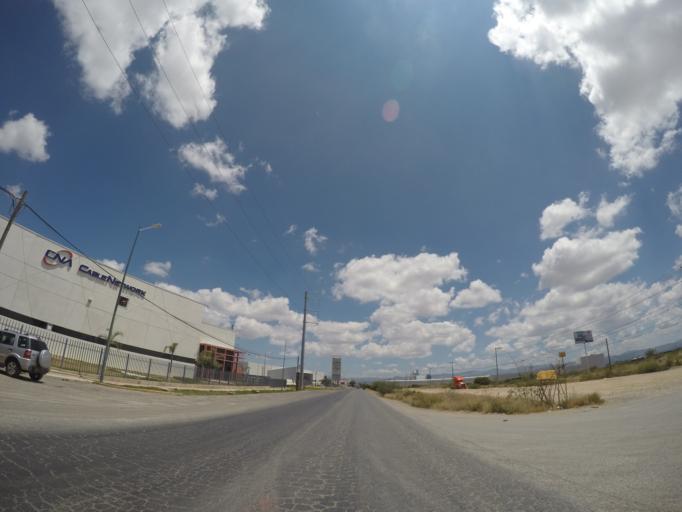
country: MX
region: San Luis Potosi
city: La Pila
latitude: 22.0419
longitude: -100.8851
